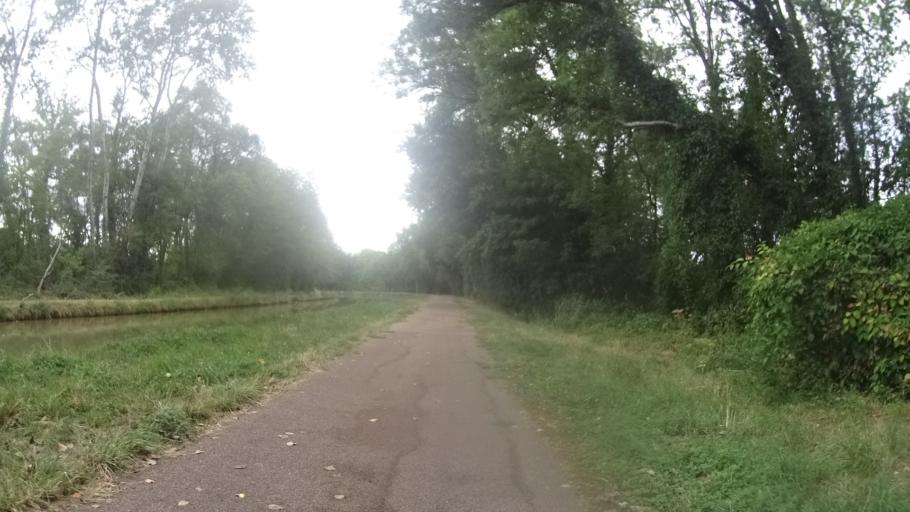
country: FR
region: Bourgogne
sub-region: Departement de la Nievre
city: Sermoise-sur-Loire
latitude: 46.9634
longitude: 3.1906
